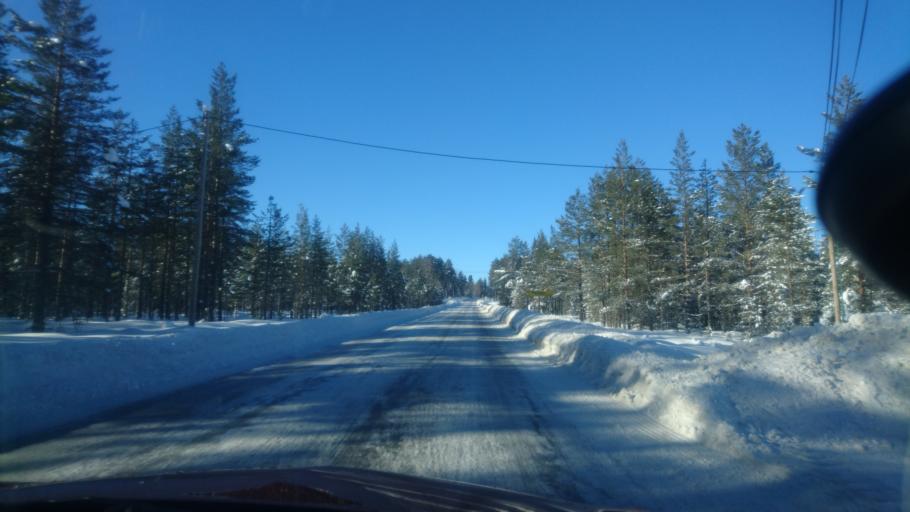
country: NO
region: Hedmark
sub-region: Trysil
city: Innbygda
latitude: 61.2510
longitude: 12.5456
